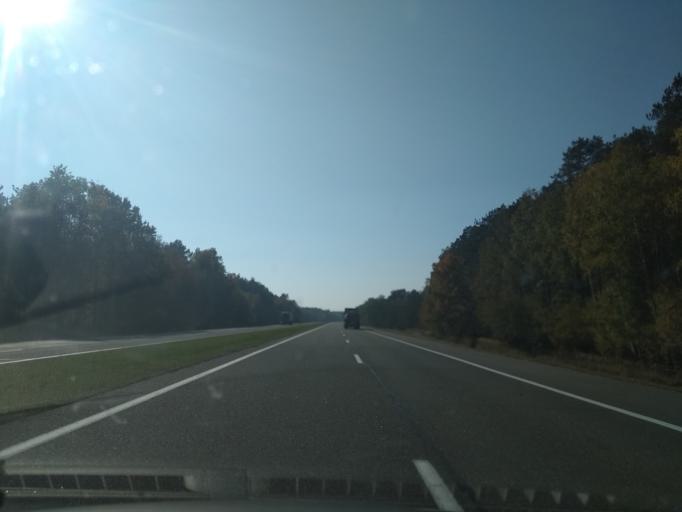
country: BY
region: Brest
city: Antopal'
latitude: 52.3725
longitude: 24.7459
